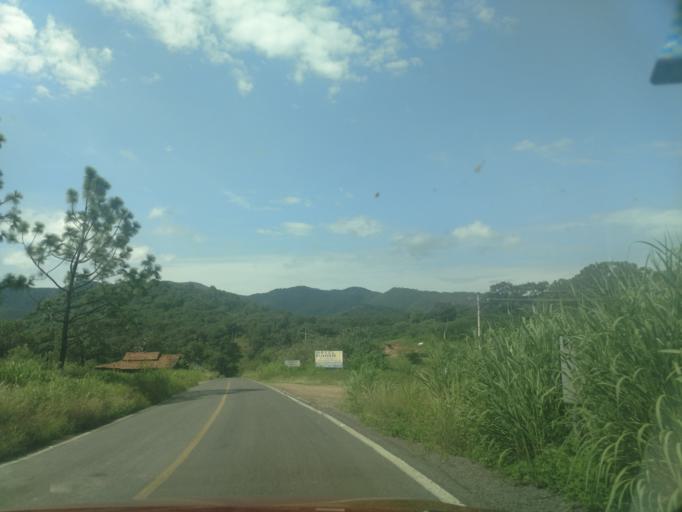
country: MX
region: Jalisco
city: Mascota
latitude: 20.4440
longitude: -104.7631
